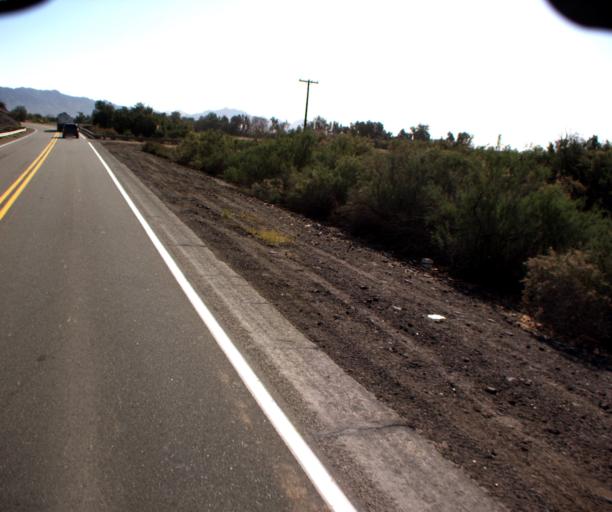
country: US
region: Arizona
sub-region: Yuma County
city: Fortuna Foothills
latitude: 32.7695
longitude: -114.3934
